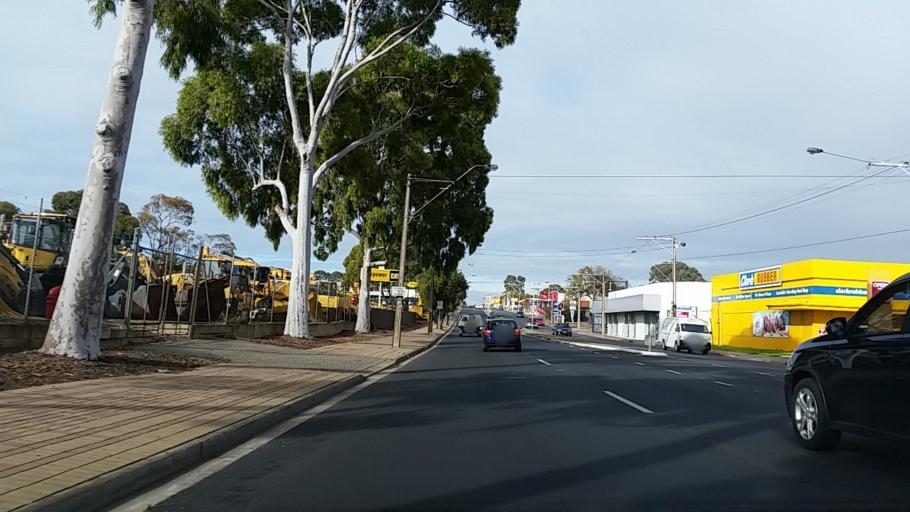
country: AU
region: South Australia
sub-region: Port Adelaide Enfield
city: Blair Athol
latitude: -34.8691
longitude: 138.6017
